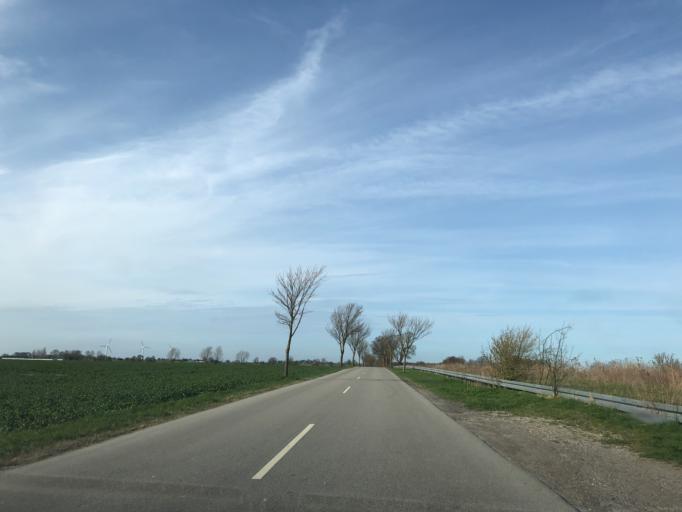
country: DK
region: Zealand
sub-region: Stevns Kommune
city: Store Heddinge
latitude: 55.3202
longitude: 12.4356
